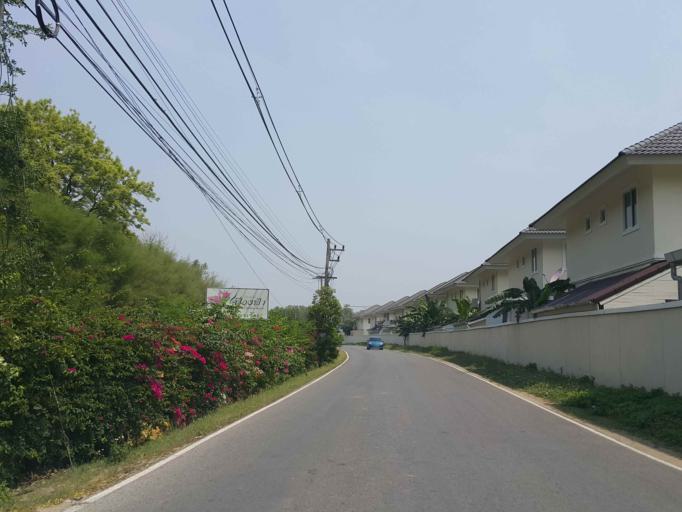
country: TH
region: Chiang Mai
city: San Sai
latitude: 18.8828
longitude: 98.9791
